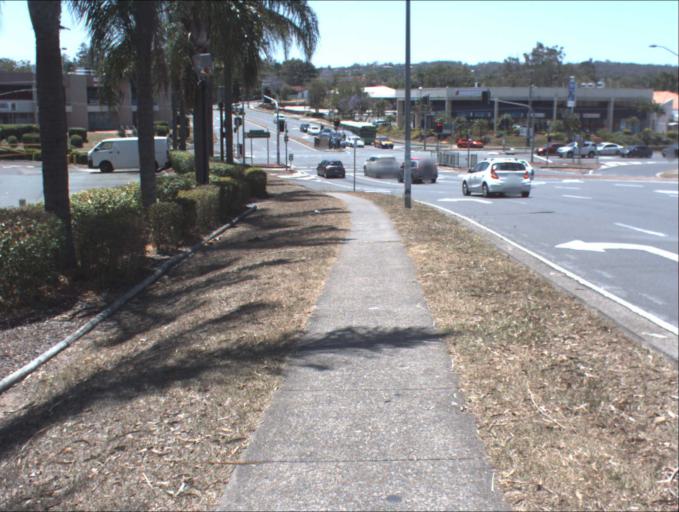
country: AU
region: Queensland
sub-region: Logan
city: Slacks Creek
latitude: -27.6633
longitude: 153.1741
